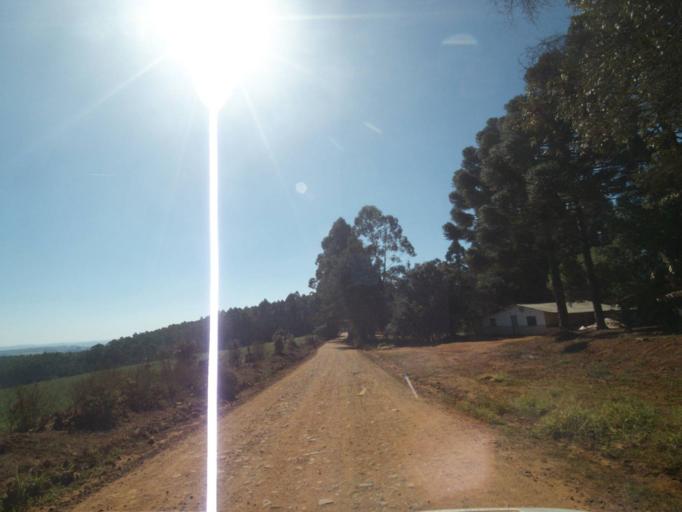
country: BR
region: Parana
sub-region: Tibagi
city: Tibagi
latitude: -24.5580
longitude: -50.6216
